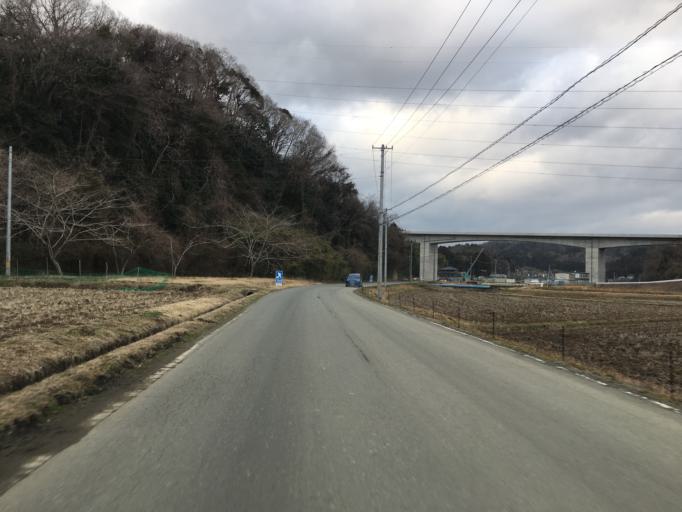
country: JP
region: Fukushima
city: Iwaki
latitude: 36.9409
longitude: 140.7906
